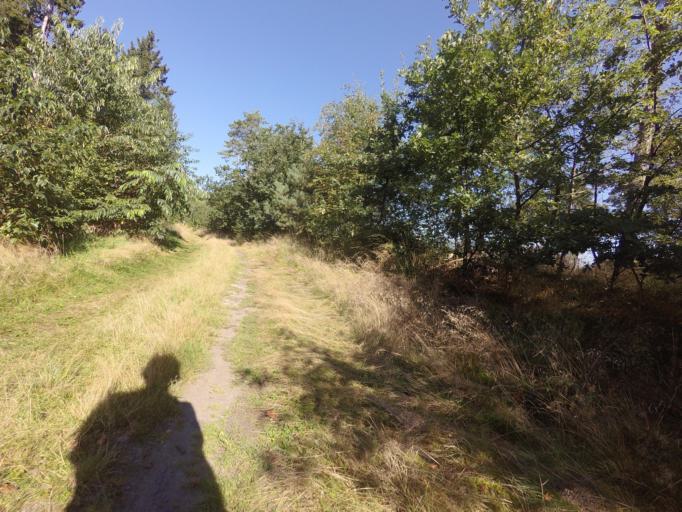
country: DE
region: Lower Saxony
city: Wielen
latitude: 52.5350
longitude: 6.7023
